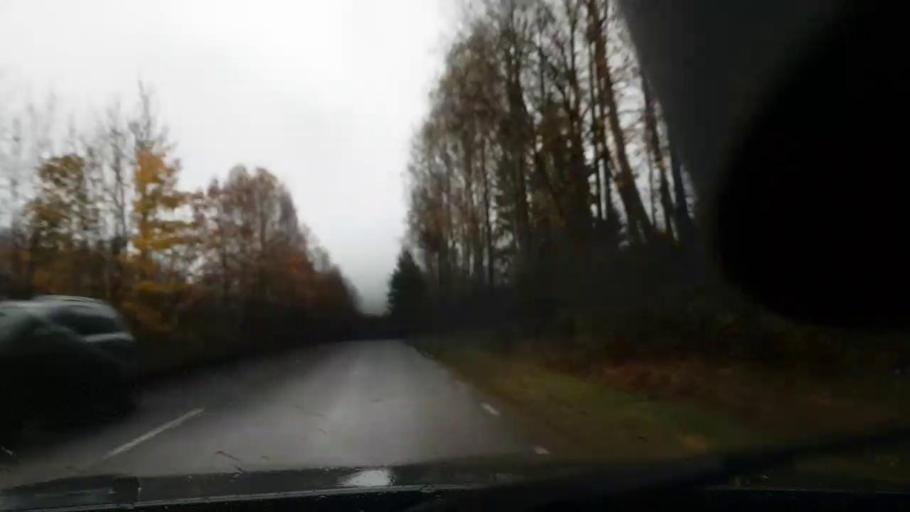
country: SE
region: Vaestra Goetaland
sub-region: Molndal
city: Lindome
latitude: 57.5944
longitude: 12.0881
